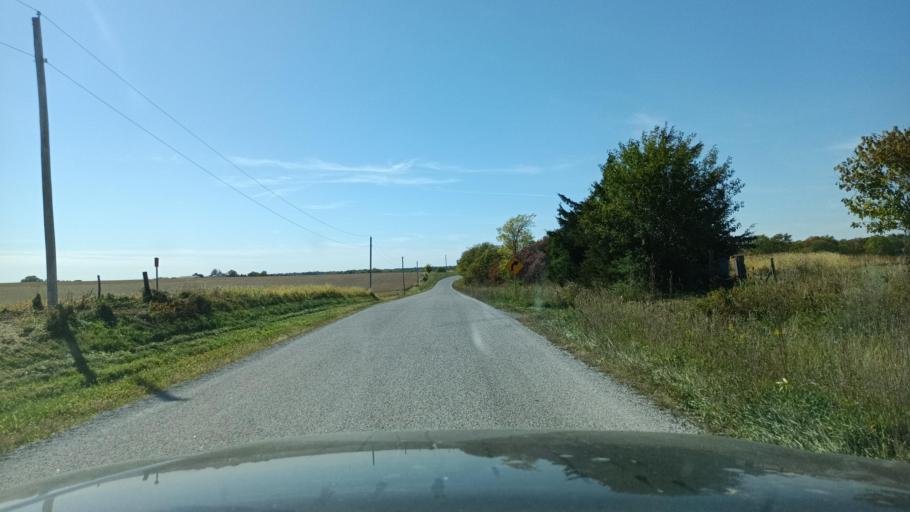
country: US
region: Illinois
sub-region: Logan County
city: Atlanta
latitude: 40.2342
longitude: -89.1522
